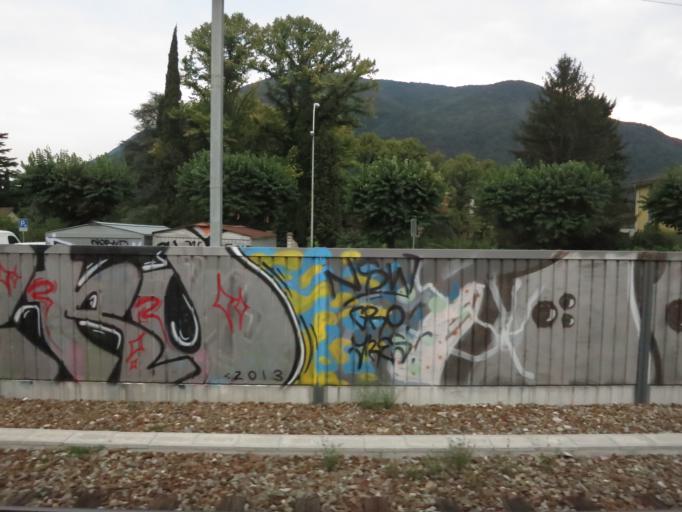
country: CH
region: Ticino
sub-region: Lugano District
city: Melano
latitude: 45.9332
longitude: 8.9730
